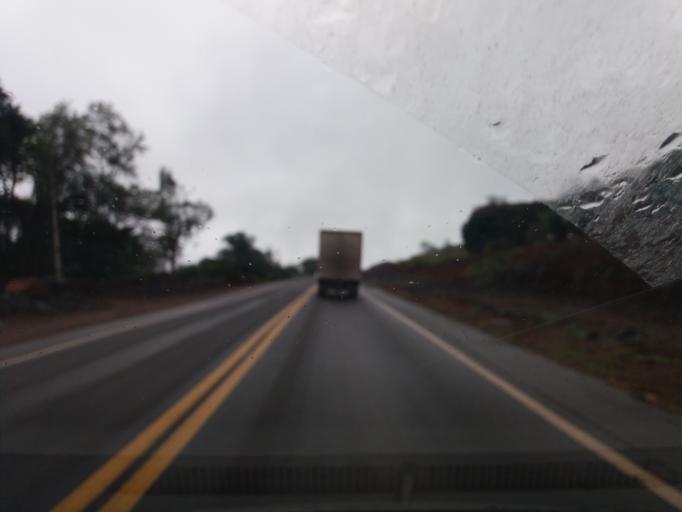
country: BR
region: Parana
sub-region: Realeza
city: Realeza
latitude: -25.4252
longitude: -53.5756
